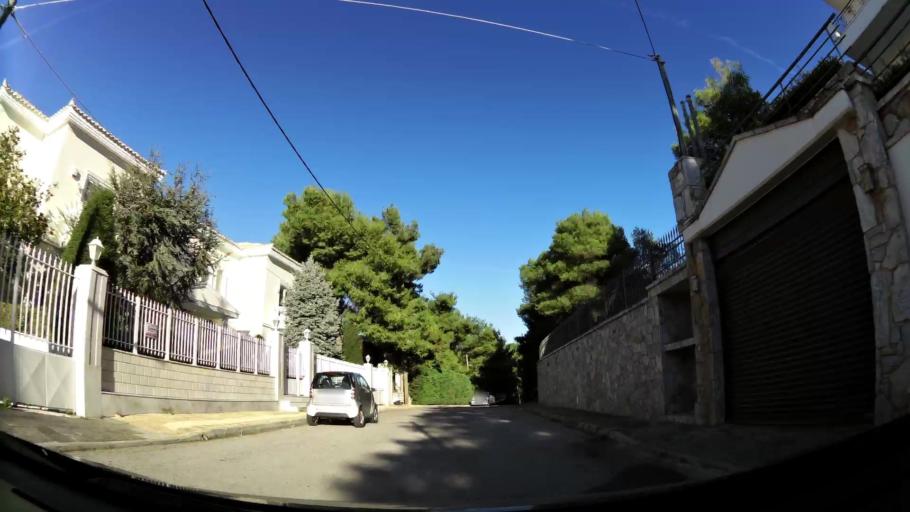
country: GR
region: Attica
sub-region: Nomarchia Athinas
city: Ekali
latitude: 38.1038
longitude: 23.8505
